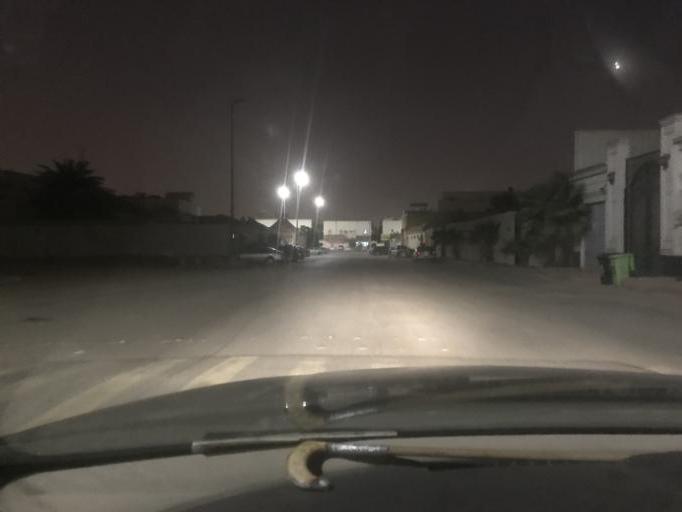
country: SA
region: Ar Riyad
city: Riyadh
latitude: 24.7356
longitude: 46.7815
